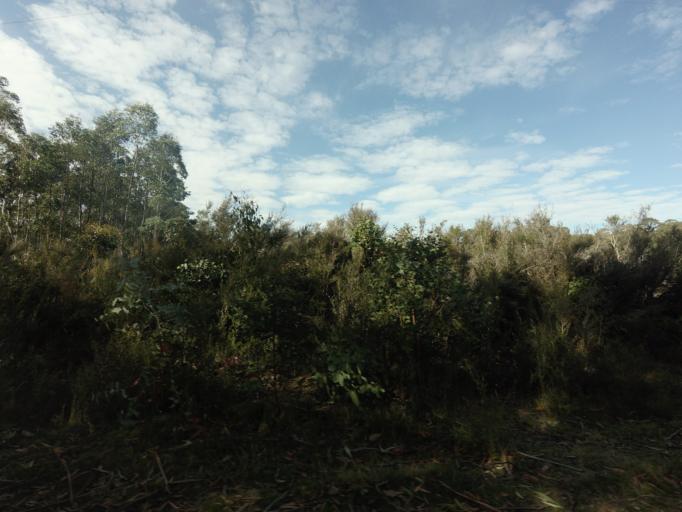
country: AU
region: Tasmania
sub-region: Sorell
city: Sorell
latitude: -42.5064
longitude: 147.4779
